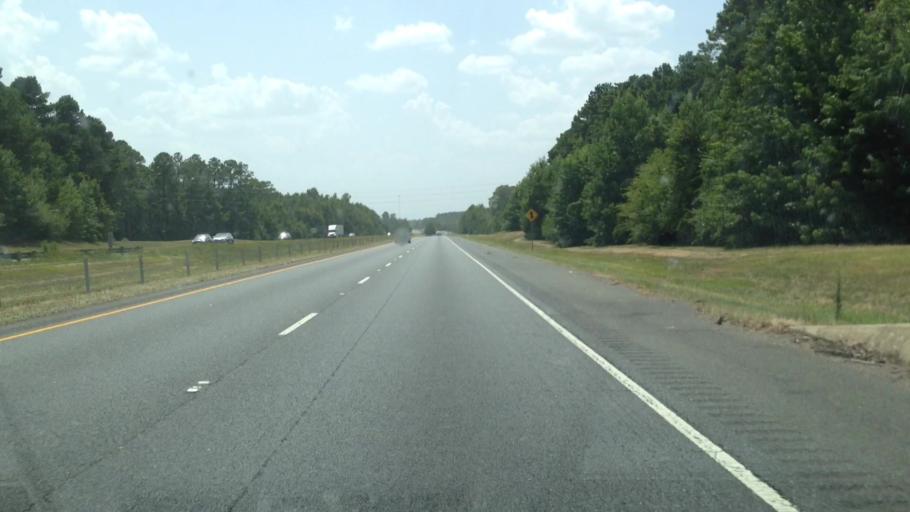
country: US
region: Louisiana
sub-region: Lincoln Parish
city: Grambling
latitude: 32.5469
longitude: -92.7667
